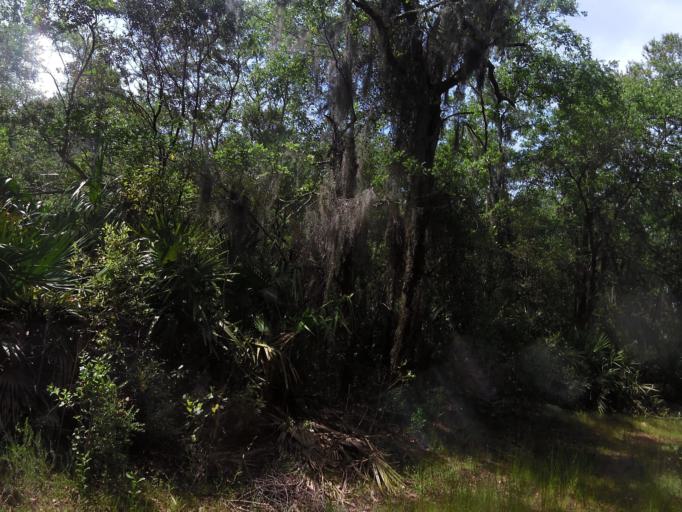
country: US
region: Florida
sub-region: Nassau County
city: Yulee
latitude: 30.4899
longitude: -81.5007
